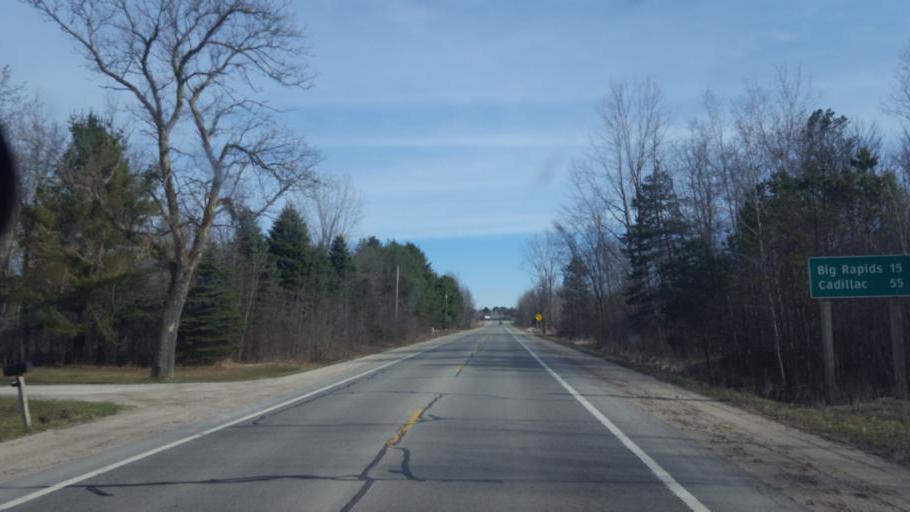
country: US
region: Michigan
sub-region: Montcalm County
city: Howard City
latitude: 43.4986
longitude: -85.4444
